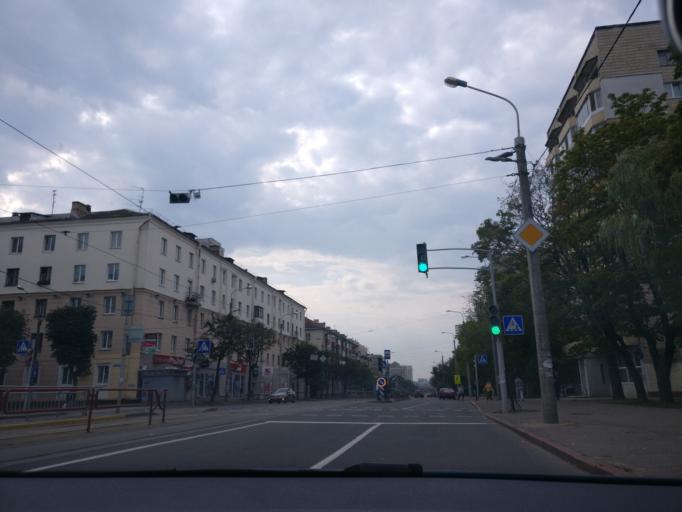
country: BY
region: Minsk
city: Minsk
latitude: 53.9289
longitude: 27.5969
